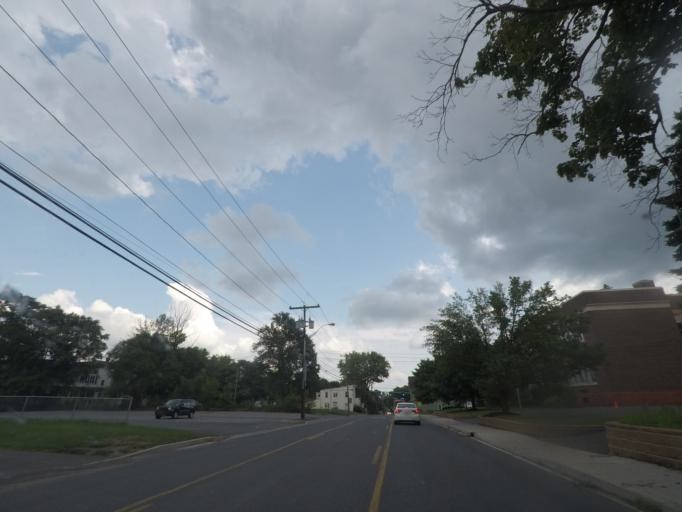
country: US
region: New York
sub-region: Albany County
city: West Albany
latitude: 42.6895
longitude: -73.7826
